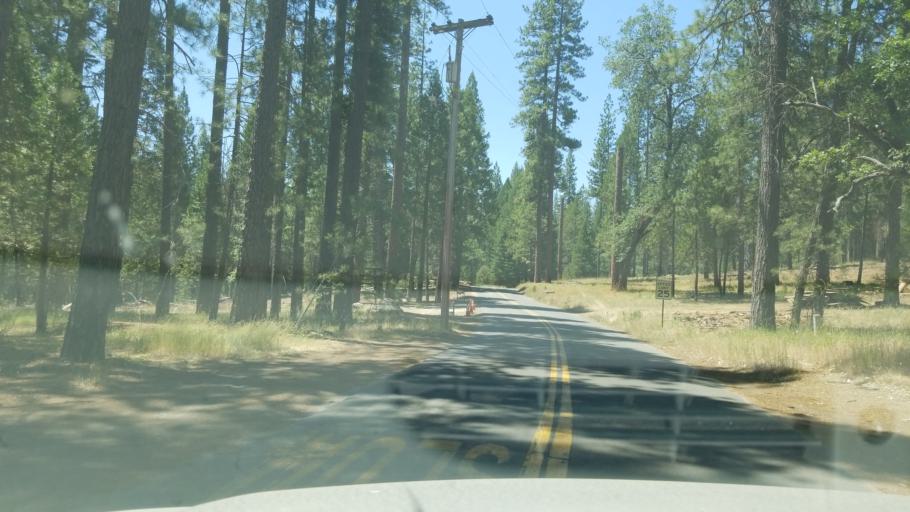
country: US
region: California
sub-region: Madera County
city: Ahwahnee
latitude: 37.5442
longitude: -119.6487
